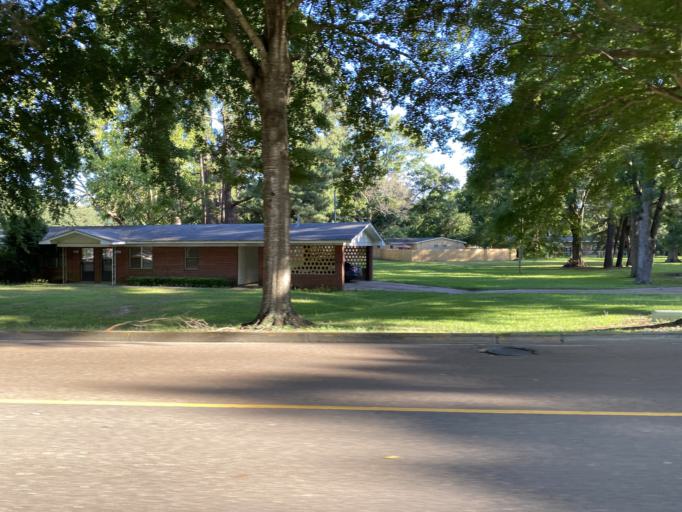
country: US
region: Mississippi
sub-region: Hinds County
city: Raymond
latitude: 32.2545
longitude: -90.4151
